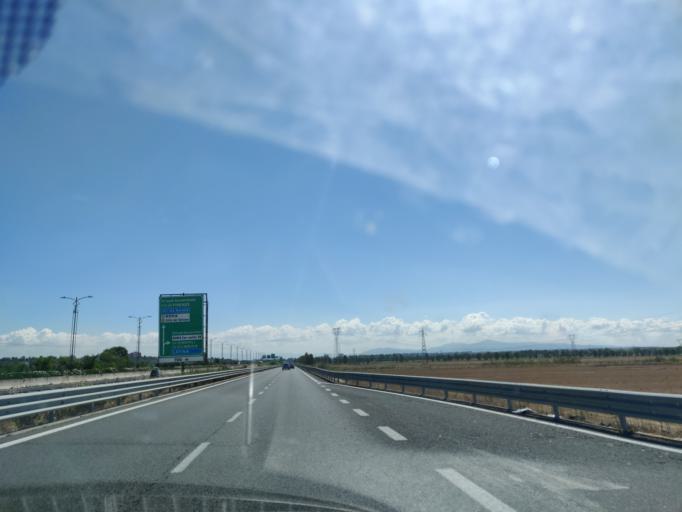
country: IT
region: Latium
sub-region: Citta metropolitana di Roma Capitale
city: Ponte Galeria-La Pisana
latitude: 41.8155
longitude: 12.3624
